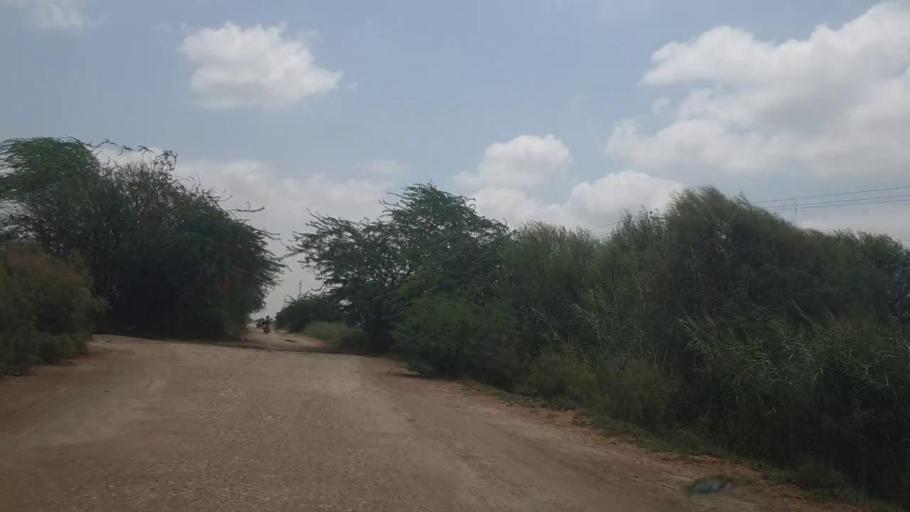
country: PK
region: Sindh
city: Tando Mittha Khan
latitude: 25.9175
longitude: 69.2164
